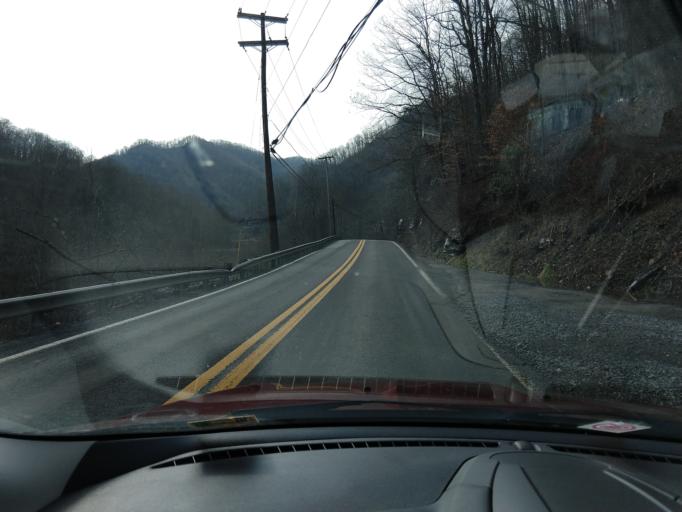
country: US
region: West Virginia
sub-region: McDowell County
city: Welch
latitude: 37.3636
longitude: -81.7987
